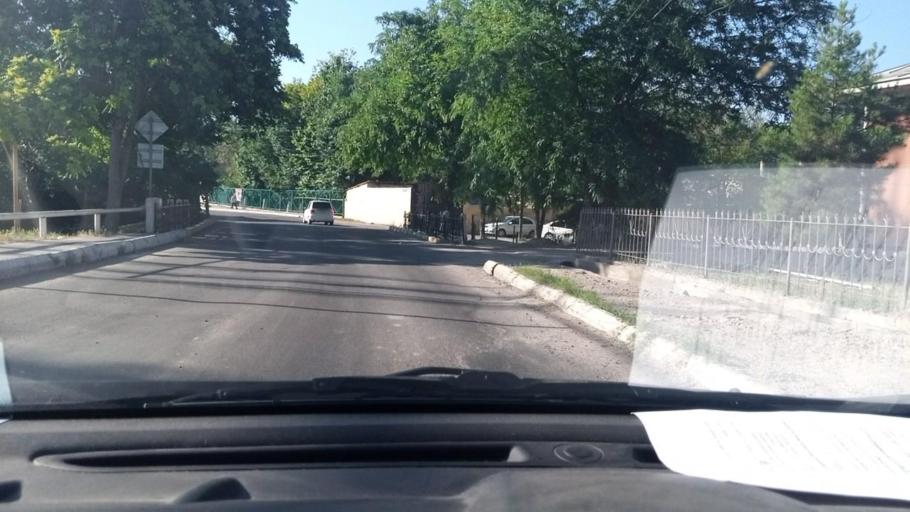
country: UZ
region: Toshkent
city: Salor
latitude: 41.3254
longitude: 69.3534
